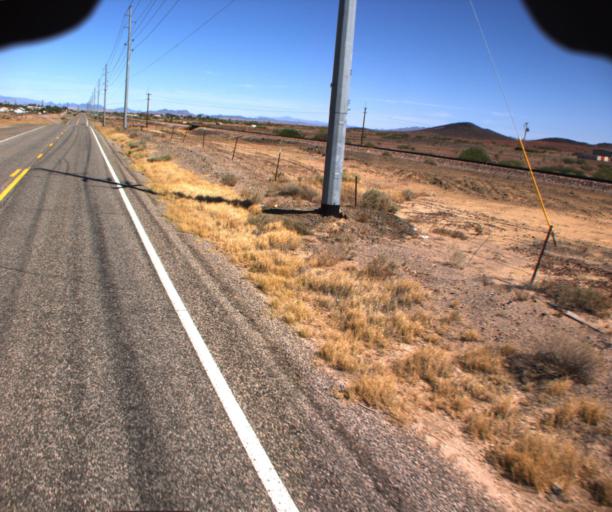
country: US
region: Arizona
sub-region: La Paz County
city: Quartzsite
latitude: 33.9184
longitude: -113.9948
